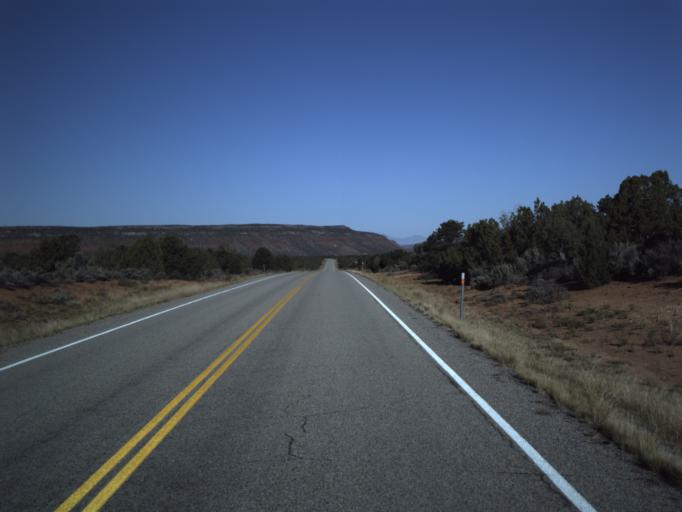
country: US
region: Utah
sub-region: San Juan County
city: Blanding
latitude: 37.5475
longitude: -109.9867
